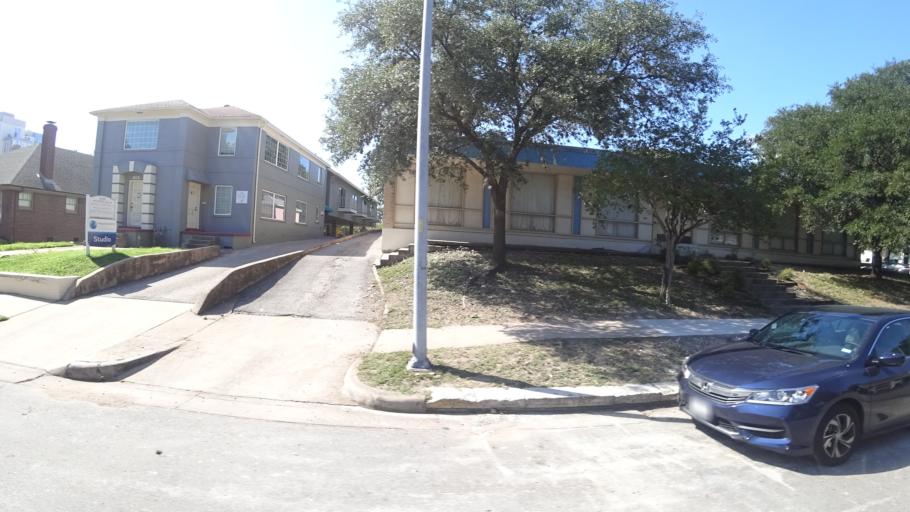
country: US
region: Texas
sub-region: Travis County
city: Austin
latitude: 30.2724
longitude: -97.7486
